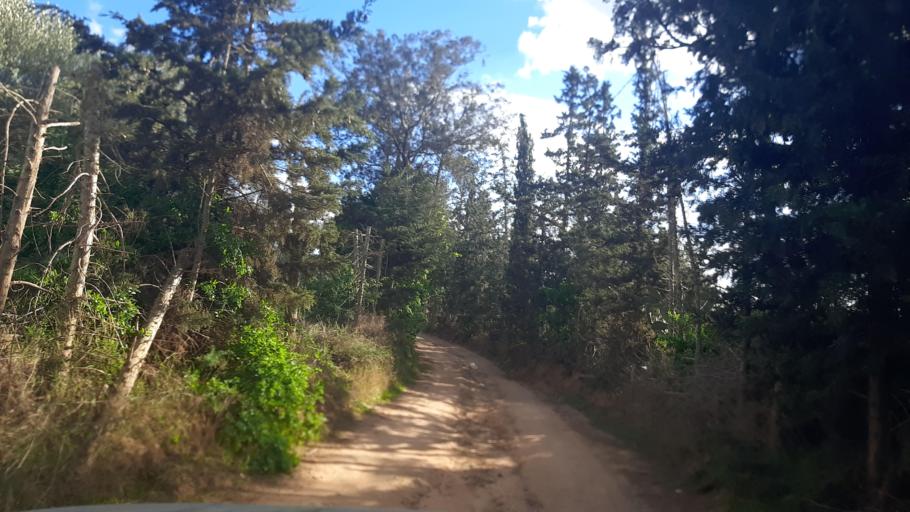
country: TN
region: Nabul
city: Bu `Urqub
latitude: 36.4327
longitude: 10.5048
